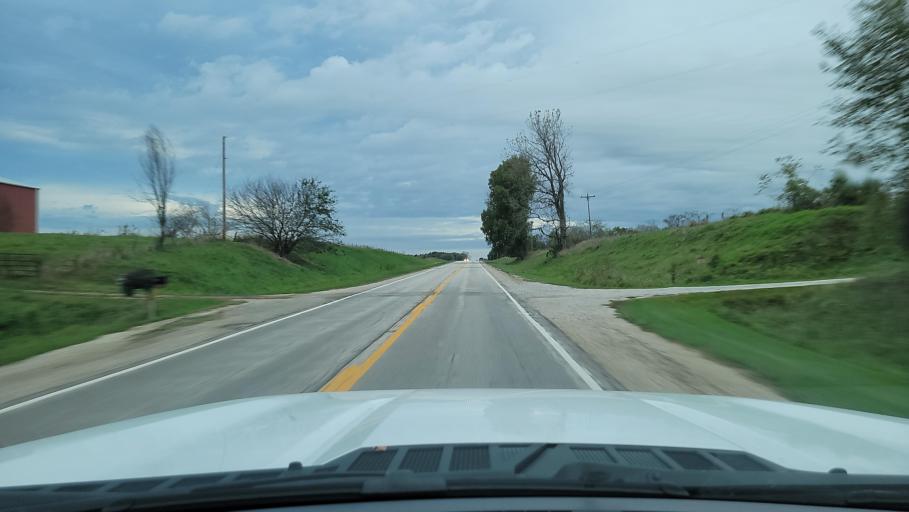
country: US
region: Illinois
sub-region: Schuyler County
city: Rushville
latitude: 40.0466
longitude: -90.6152
